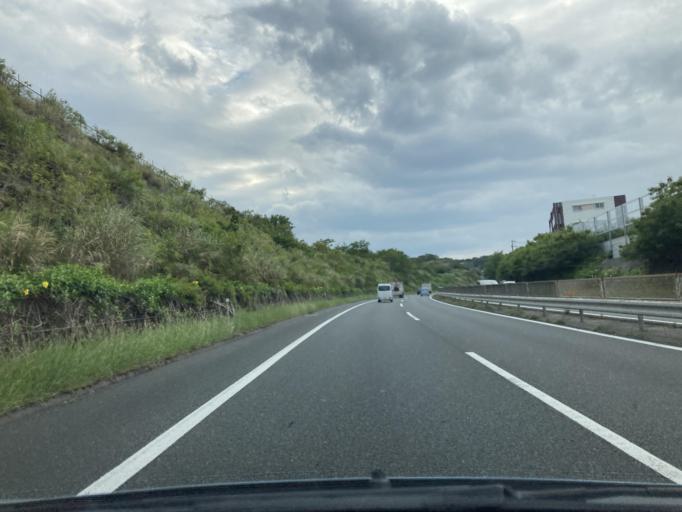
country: JP
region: Okinawa
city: Ginowan
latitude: 26.2514
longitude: 127.7606
